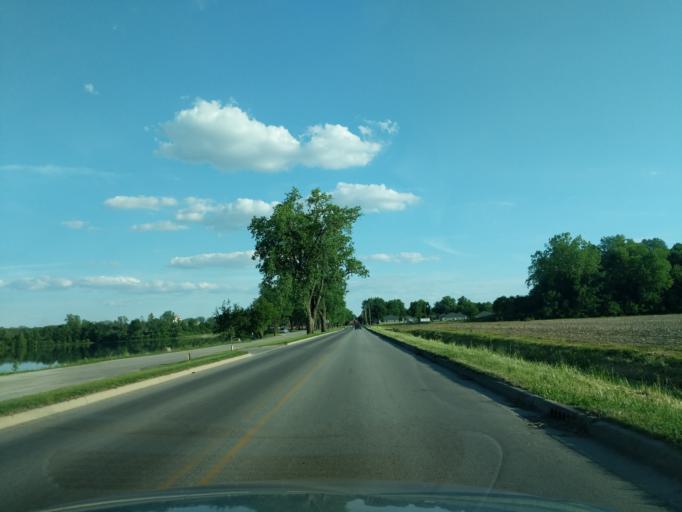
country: US
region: Indiana
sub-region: Huntington County
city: Huntington
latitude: 40.8948
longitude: -85.4713
